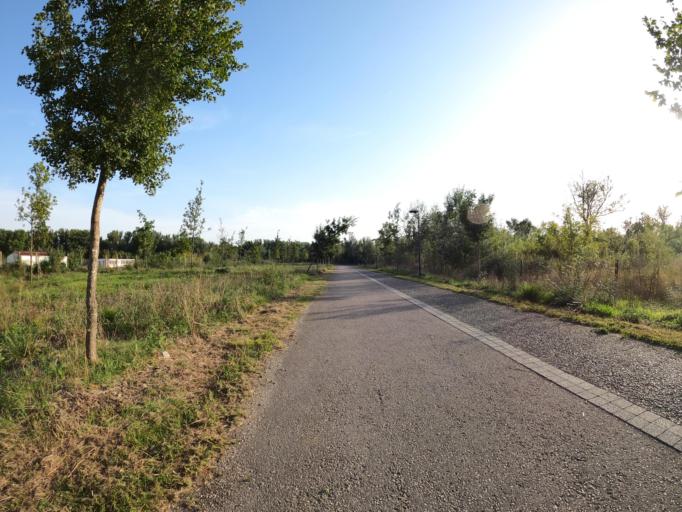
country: FR
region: Midi-Pyrenees
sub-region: Departement de la Haute-Garonne
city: Vieille-Toulouse
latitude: 43.5513
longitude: 1.4301
